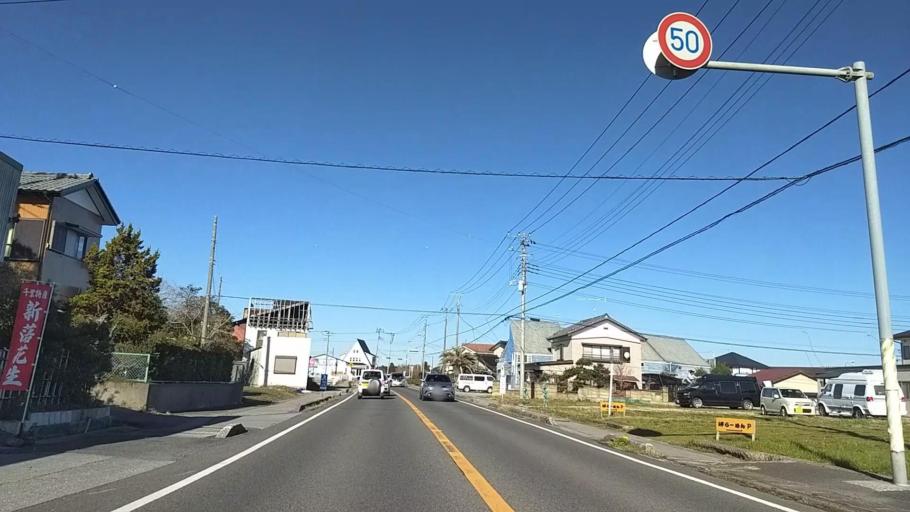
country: JP
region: Chiba
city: Ohara
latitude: 35.2957
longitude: 140.3958
